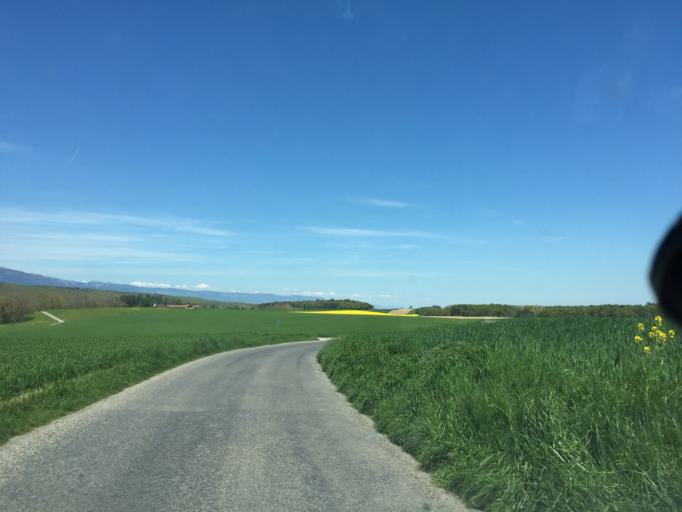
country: CH
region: Vaud
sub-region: Morges District
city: Cuarnens
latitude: 46.6265
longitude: 6.4434
